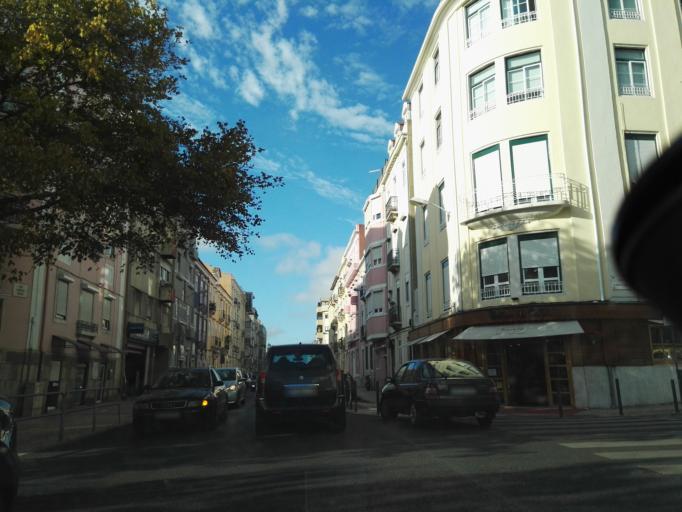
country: PT
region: Lisbon
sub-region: Lisbon
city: Lisbon
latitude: 38.7173
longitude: -9.1695
